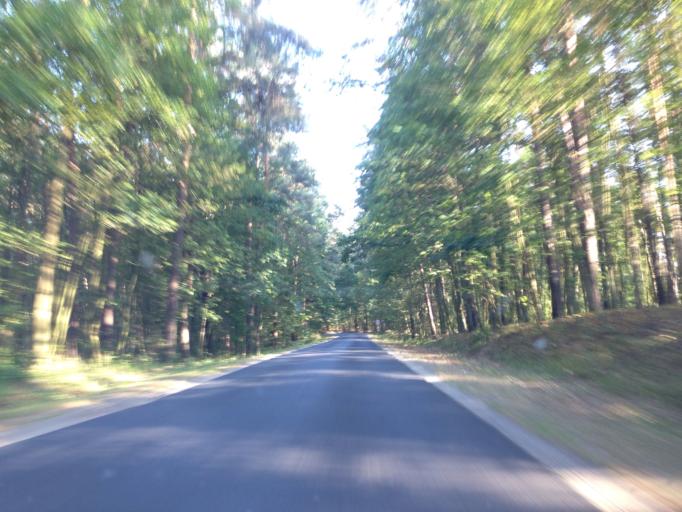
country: PL
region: Kujawsko-Pomorskie
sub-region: Powiat brodnicki
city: Brodnica
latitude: 53.3593
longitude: 19.3840
